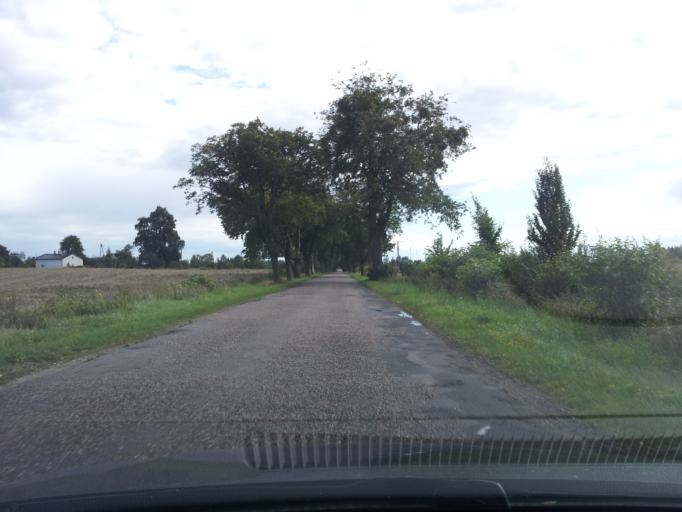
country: PL
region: Kujawsko-Pomorskie
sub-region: Powiat brodnicki
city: Gorzno
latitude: 53.2190
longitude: 19.6344
